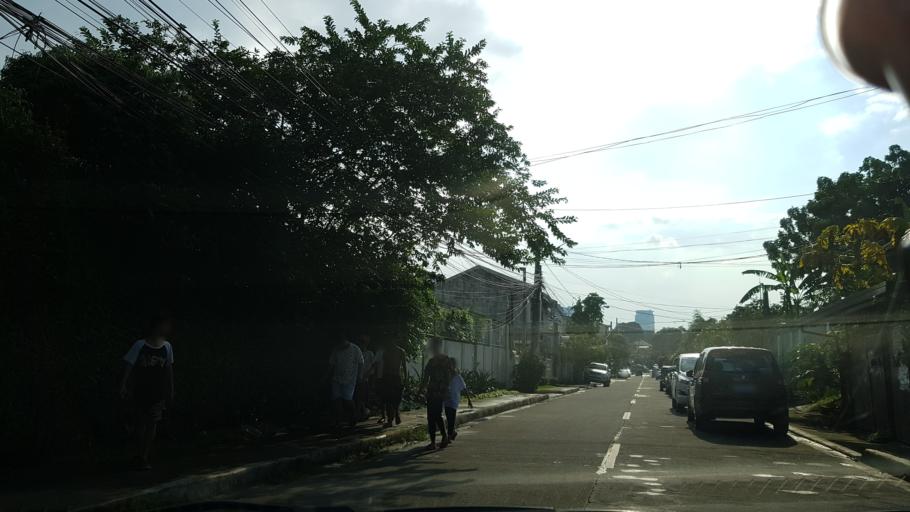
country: PH
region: Metro Manila
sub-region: Quezon City
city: Quezon City
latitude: 14.6421
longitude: 121.0530
